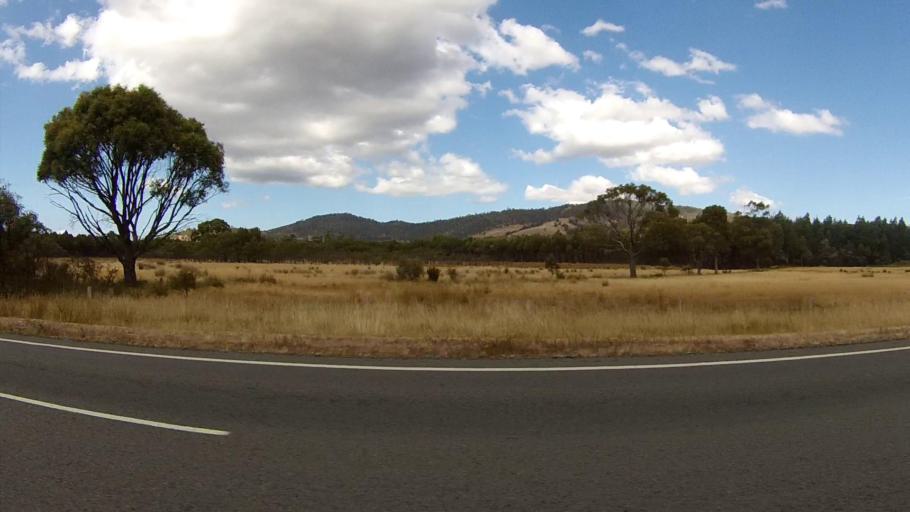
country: AU
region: Tasmania
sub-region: Sorell
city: Sorell
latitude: -42.6410
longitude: 147.5797
